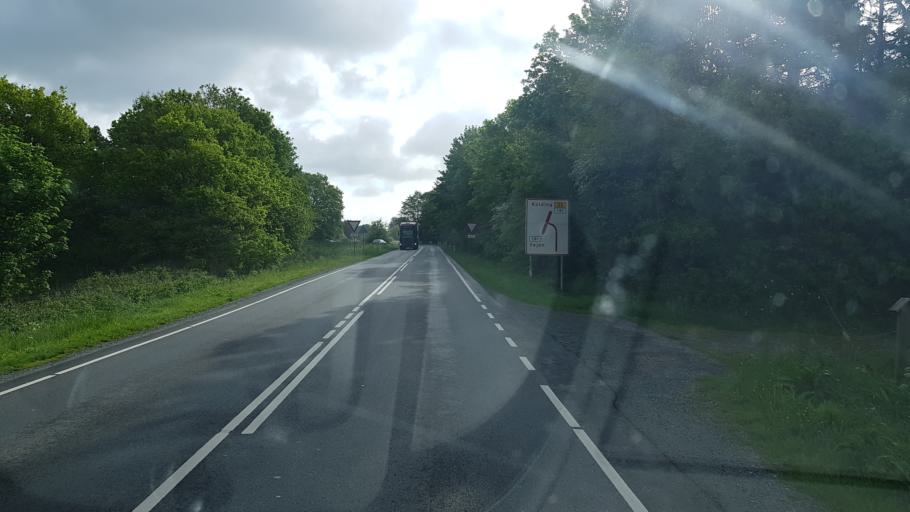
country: DK
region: South Denmark
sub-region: Vejen Kommune
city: Vejen
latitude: 55.4679
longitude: 9.1805
